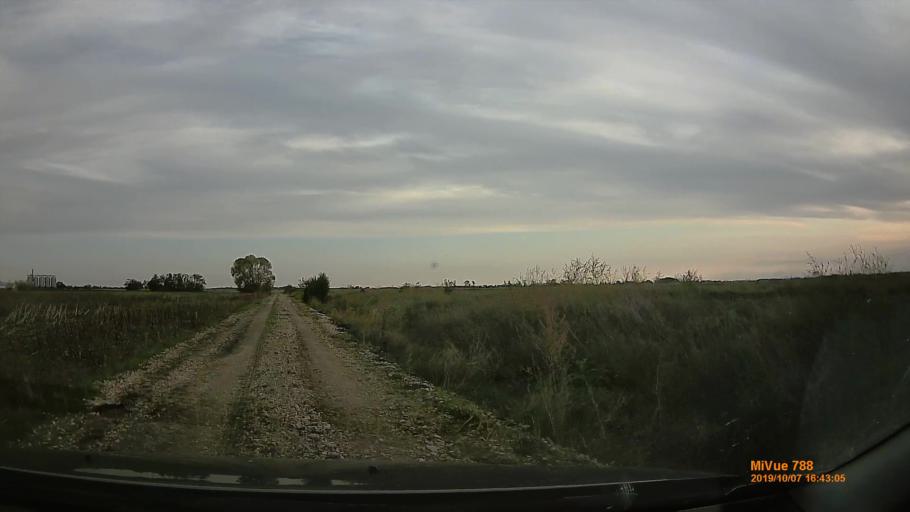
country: HU
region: Bekes
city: Szarvas
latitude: 46.8151
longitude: 20.6036
